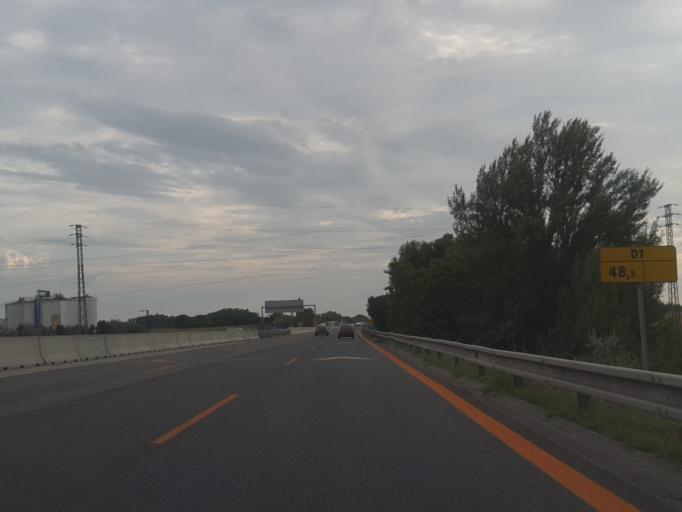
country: SK
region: Trnavsky
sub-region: Okres Trnava
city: Trnava
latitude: 48.3298
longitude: 17.6168
